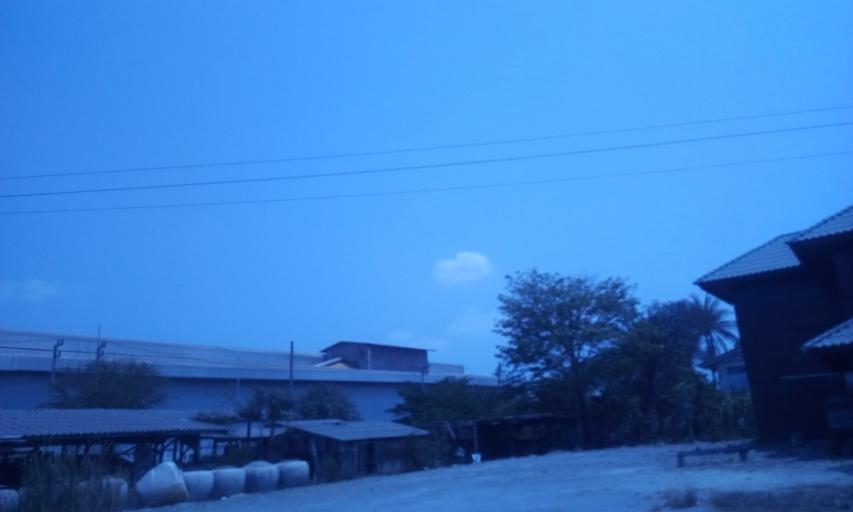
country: TH
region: Chachoengsao
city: Bang Nam Priao
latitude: 13.9510
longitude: 100.9738
